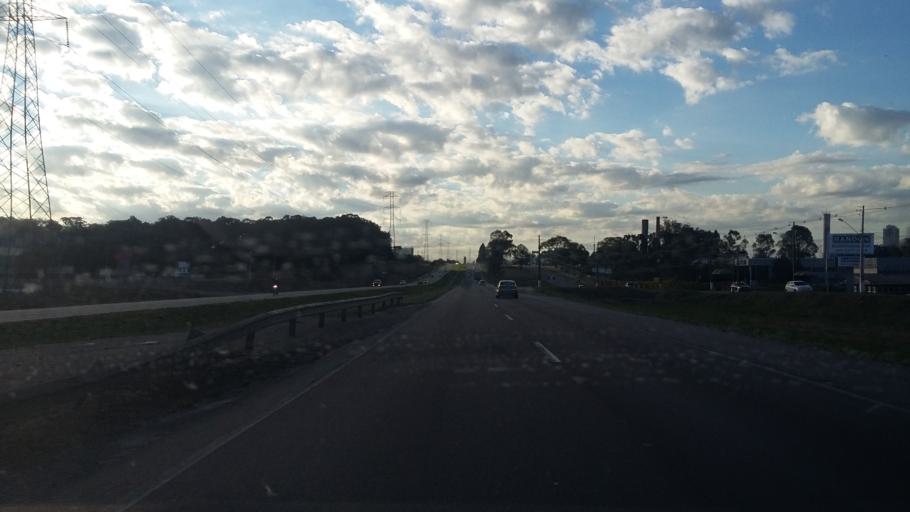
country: BR
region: Parana
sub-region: Curitiba
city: Curitiba
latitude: -25.4644
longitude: -49.3571
